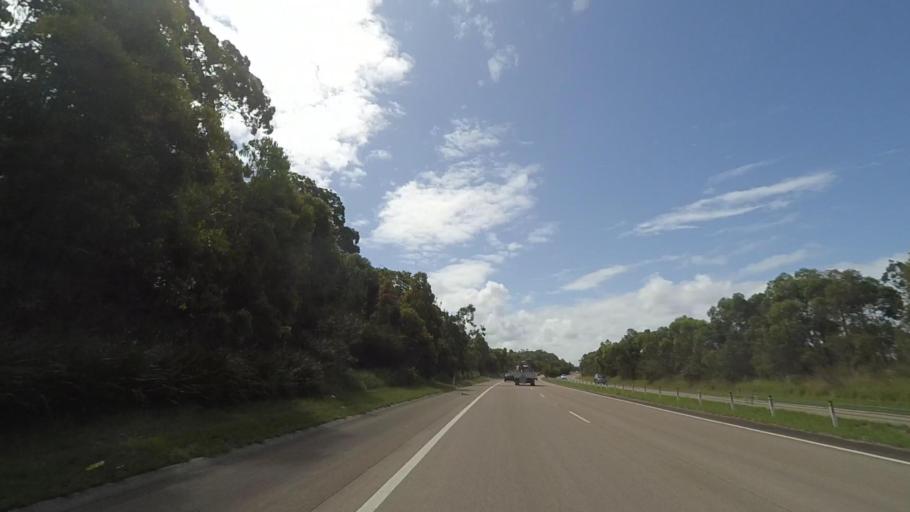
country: AU
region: New South Wales
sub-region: Lake Macquarie Shire
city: Gateshead
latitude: -32.9814
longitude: 151.6808
